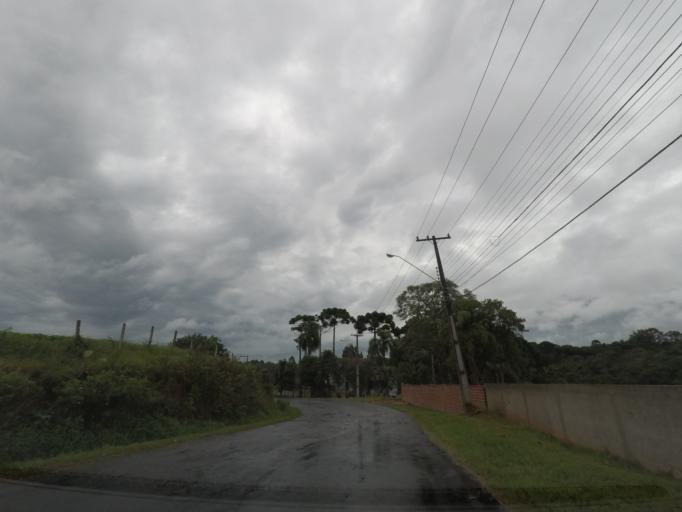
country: BR
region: Parana
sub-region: Campo Largo
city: Campo Largo
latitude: -25.4508
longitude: -49.4391
